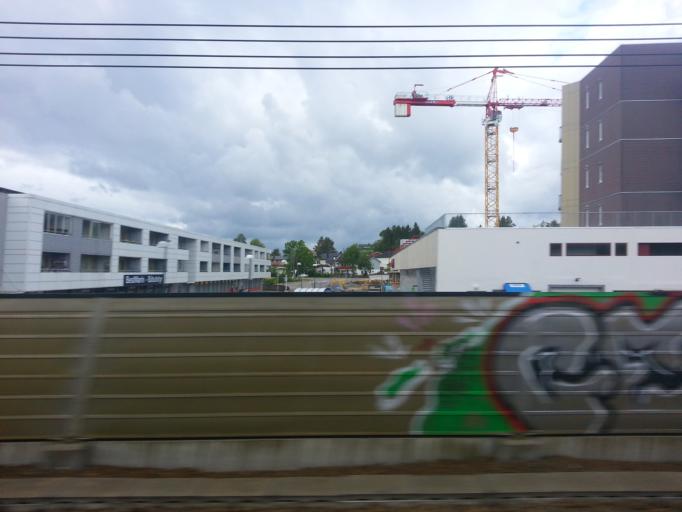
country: NO
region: Akershus
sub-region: Skedsmo
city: Lillestrom
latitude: 59.9642
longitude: 11.0659
